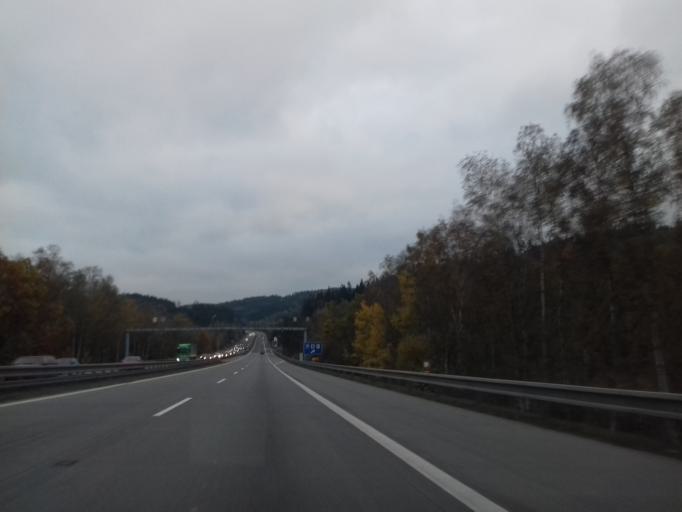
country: CZ
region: Central Bohemia
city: Divisov
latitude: 49.7843
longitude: 14.9298
